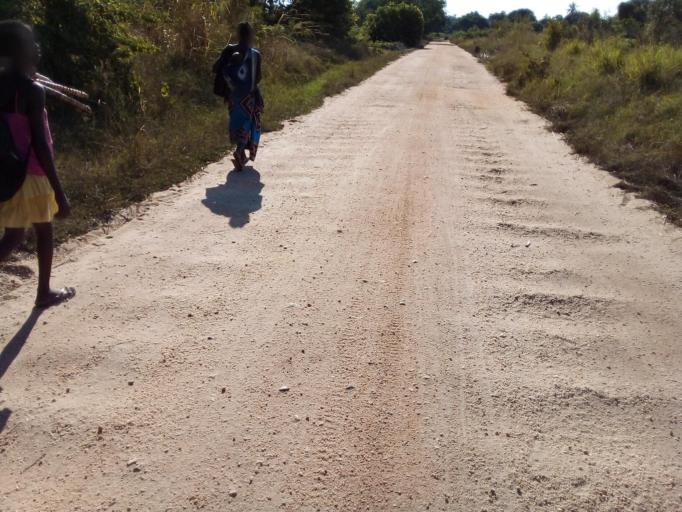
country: MZ
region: Zambezia
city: Quelimane
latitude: -17.5290
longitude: 36.6182
